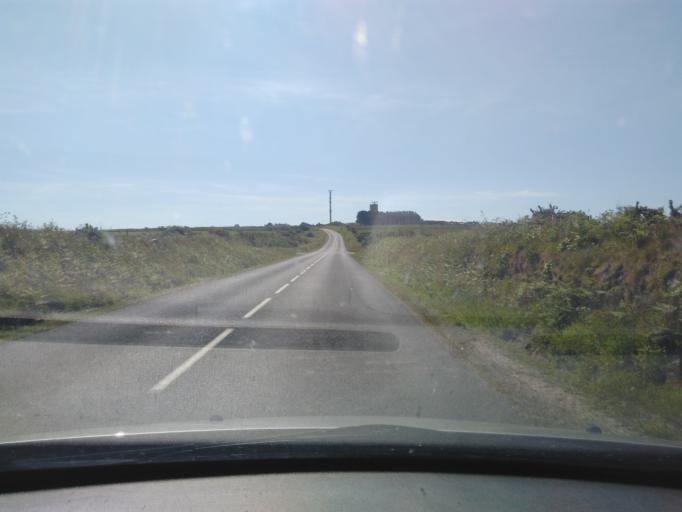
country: FR
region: Lower Normandy
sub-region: Departement de la Manche
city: Beaumont-Hague
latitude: 49.6886
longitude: -1.9128
